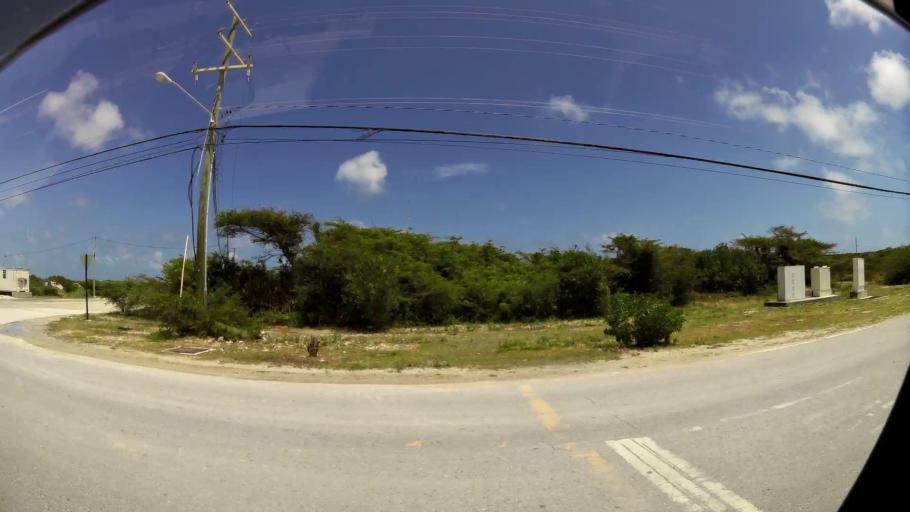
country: TC
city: Cockburn Town
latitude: 21.4370
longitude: -71.1470
